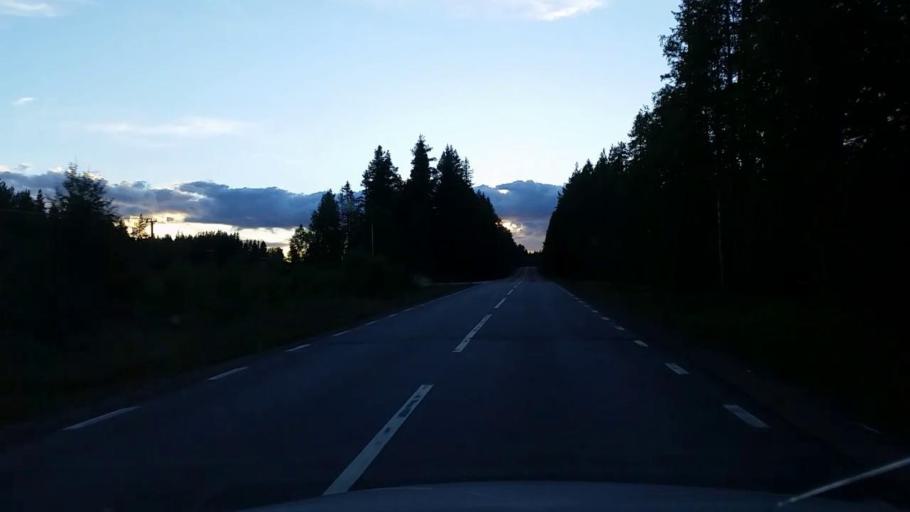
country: SE
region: Gaevleborg
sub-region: Ljusdals Kommun
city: Farila
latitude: 62.0874
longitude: 15.8092
